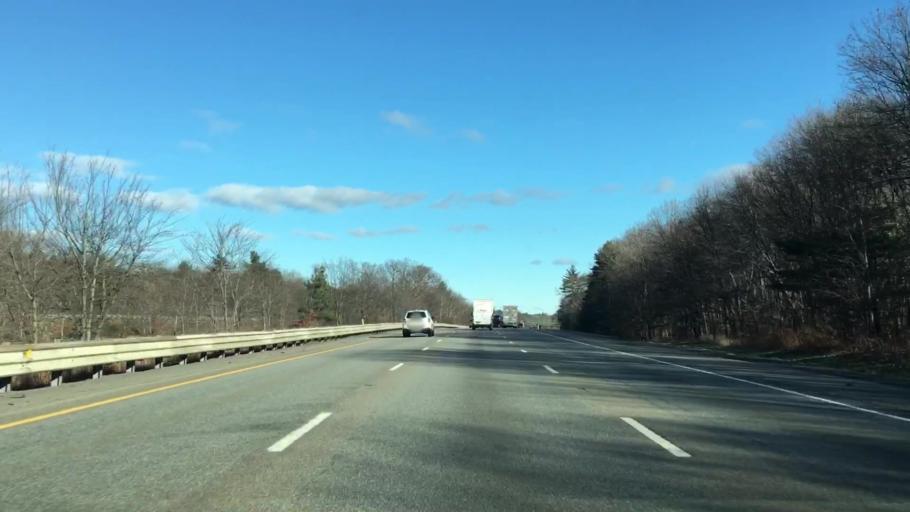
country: US
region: Massachusetts
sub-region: Worcester County
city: Bolton
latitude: 42.4449
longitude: -71.5859
